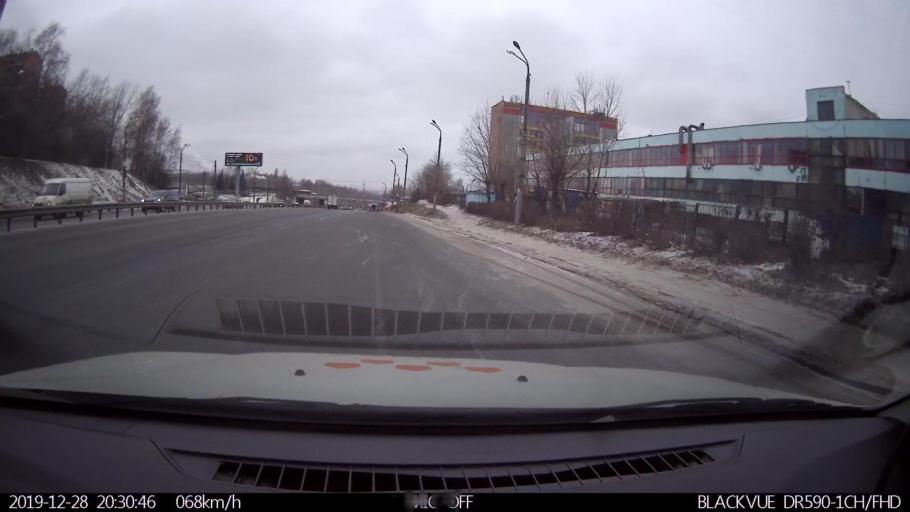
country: RU
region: Nizjnij Novgorod
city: Nizhniy Novgorod
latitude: 56.2419
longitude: 43.9696
